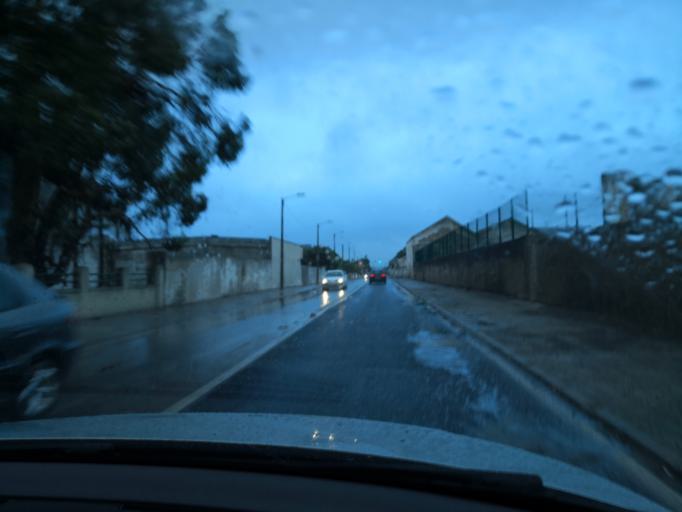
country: PT
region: Setubal
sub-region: Moita
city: Alhos Vedros
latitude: 38.6532
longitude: -9.0237
